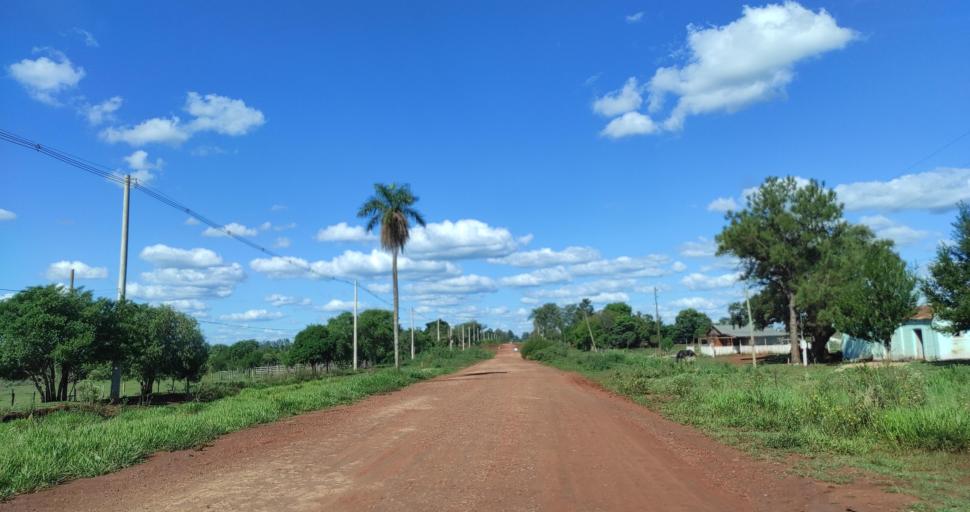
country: AR
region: Misiones
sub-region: Departamento de Candelaria
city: Candelaria
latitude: -27.4633
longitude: -55.7281
